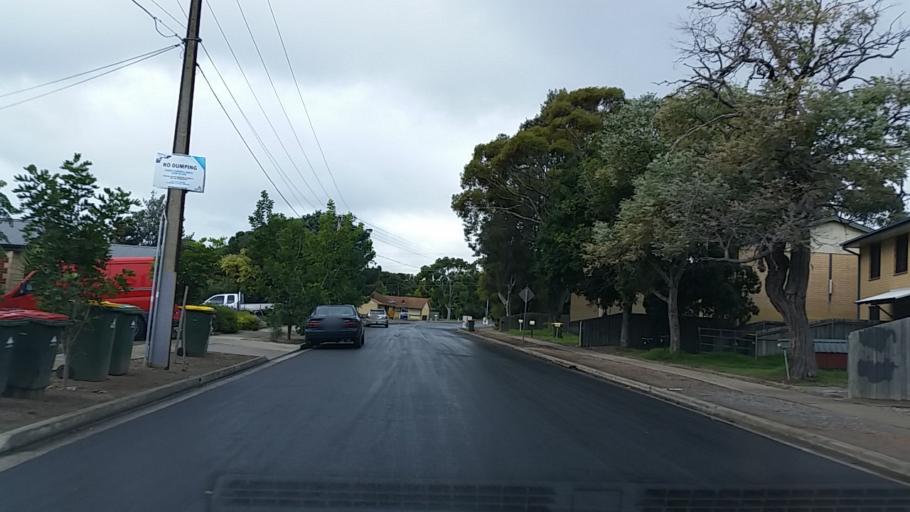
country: AU
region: South Australia
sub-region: Marion
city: Sturt
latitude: -35.0218
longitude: 138.5519
